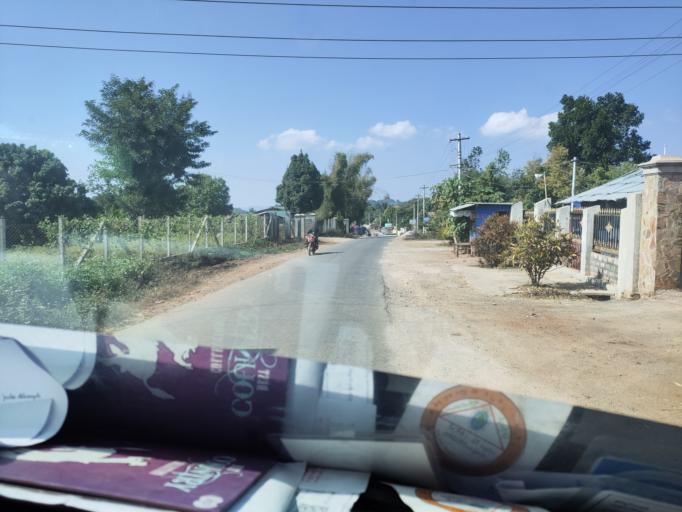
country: MM
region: Mandalay
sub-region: Pyin Oo Lwin District
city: Pyin Oo Lwin
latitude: 21.9525
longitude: 96.3957
